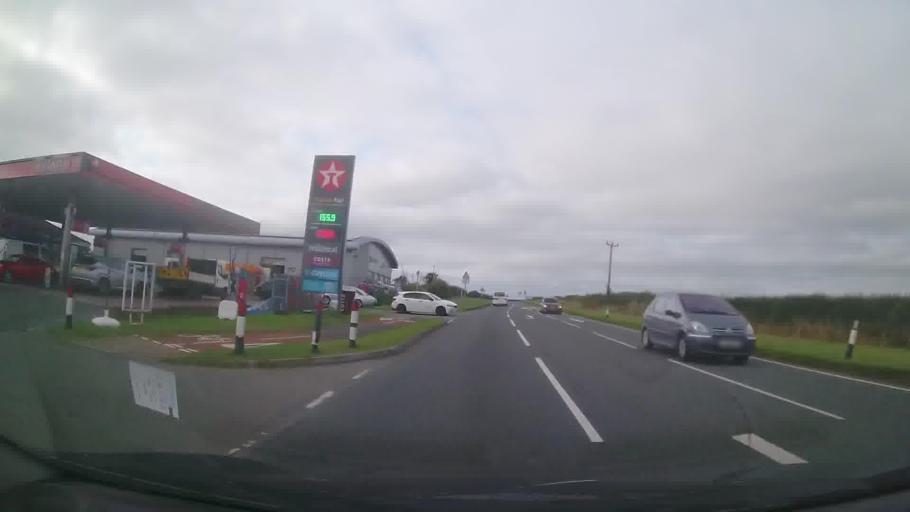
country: GB
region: Wales
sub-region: Pembrokeshire
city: Neyland
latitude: 51.7193
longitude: -4.9629
